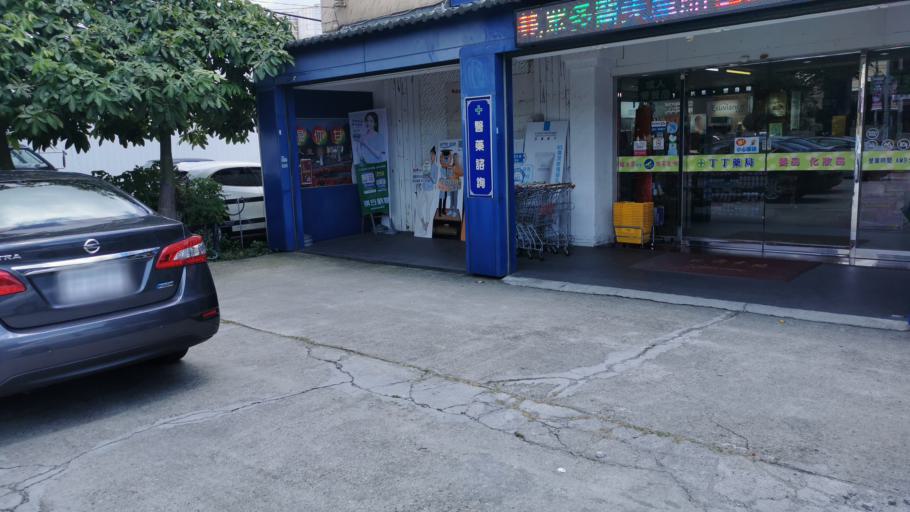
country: TW
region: Taiwan
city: Fengyuan
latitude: 24.2158
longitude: 120.7025
